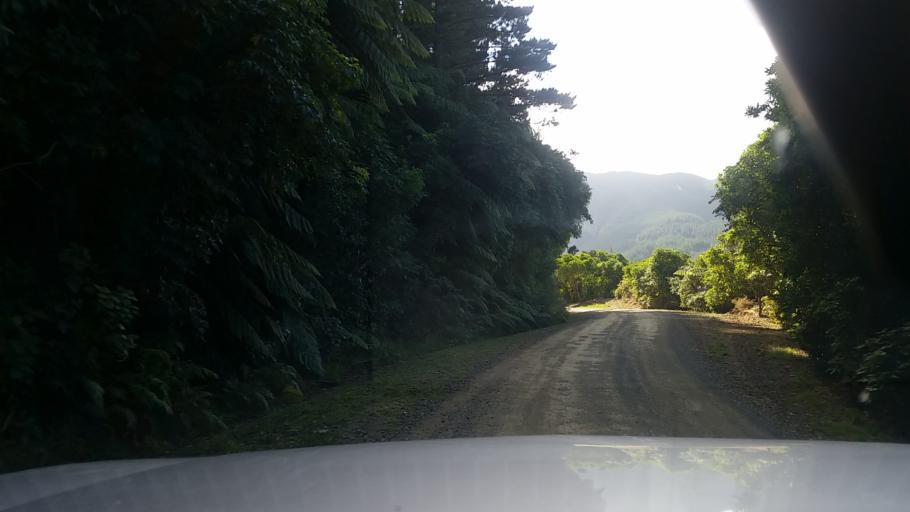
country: NZ
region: Marlborough
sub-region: Marlborough District
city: Picton
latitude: -41.2884
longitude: 174.1725
